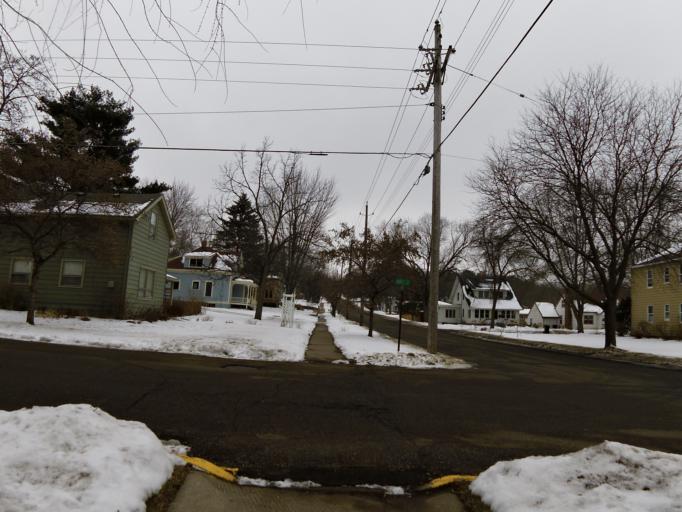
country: US
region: Wisconsin
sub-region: Saint Croix County
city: Hudson
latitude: 44.9796
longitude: -92.7464
